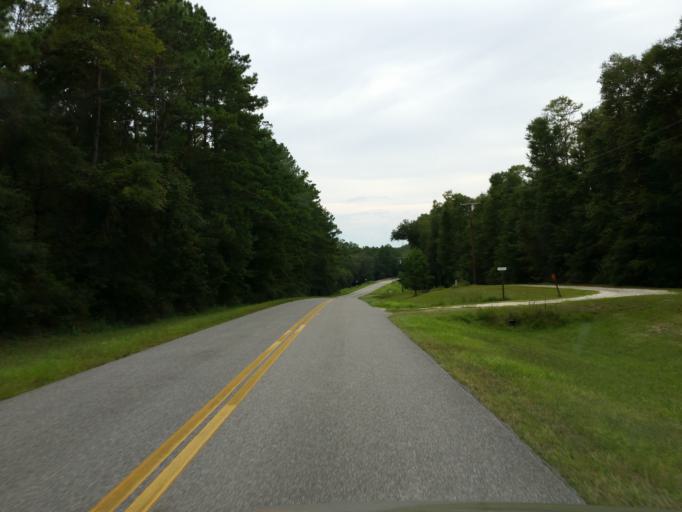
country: US
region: Florida
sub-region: Alachua County
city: High Springs
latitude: 29.9506
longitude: -82.5261
